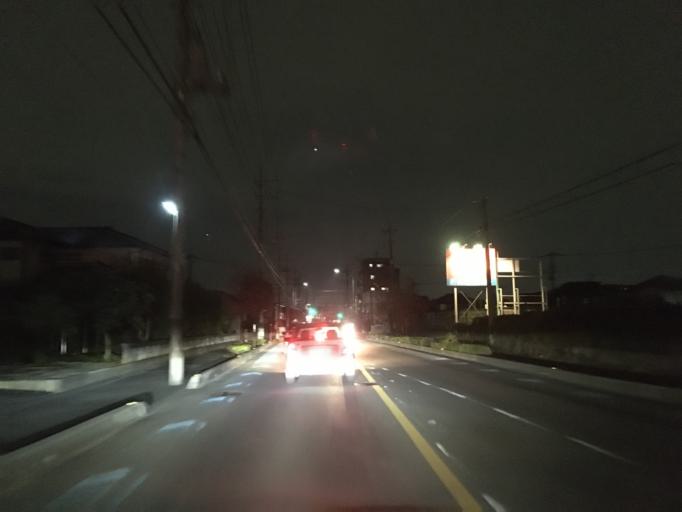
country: JP
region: Saitama
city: Sayama
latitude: 35.8396
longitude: 139.4252
